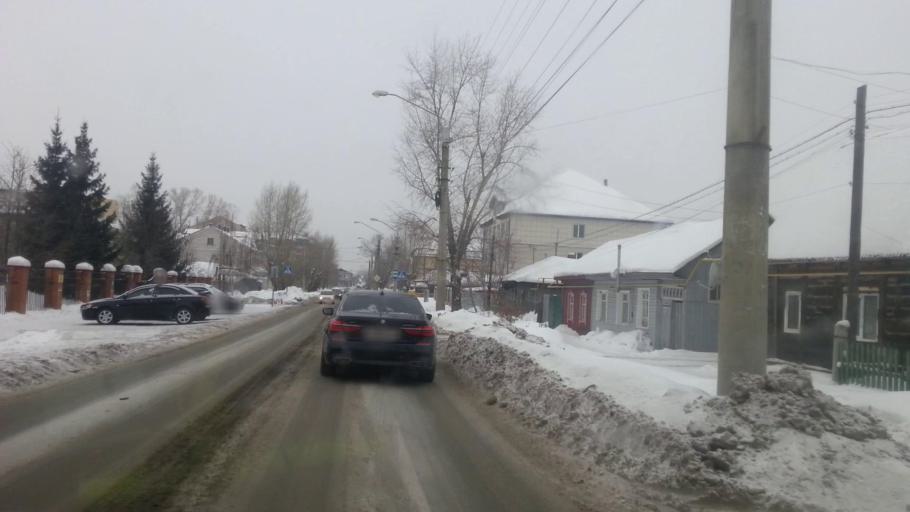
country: RU
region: Altai Krai
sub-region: Gorod Barnaulskiy
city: Barnaul
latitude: 53.3323
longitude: 83.7660
